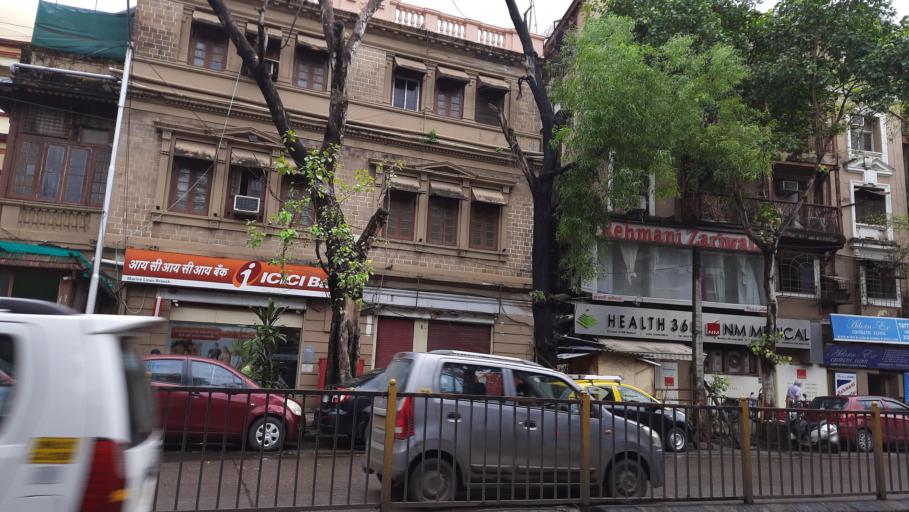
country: IN
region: Maharashtra
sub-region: Raigarh
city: Uran
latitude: 18.9434
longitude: 72.8255
